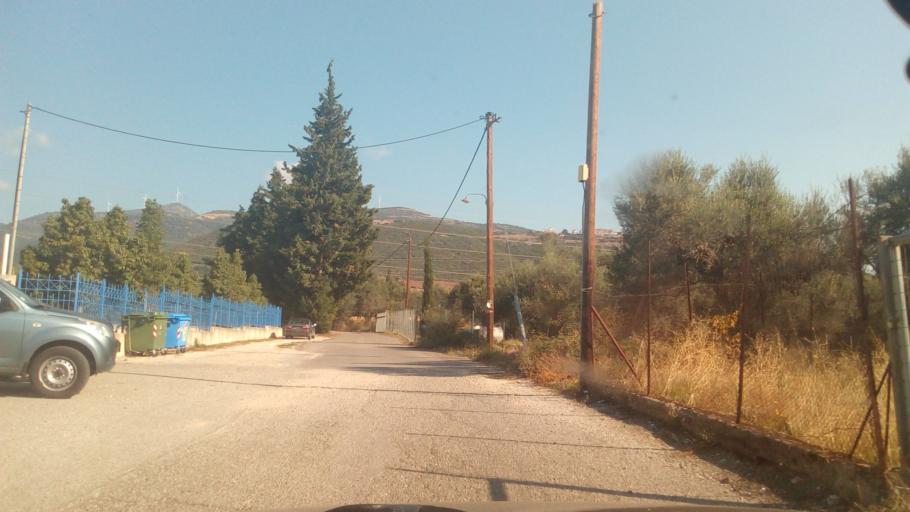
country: GR
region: West Greece
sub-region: Nomos Aitolias kai Akarnanias
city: Nafpaktos
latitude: 38.4026
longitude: 21.8463
